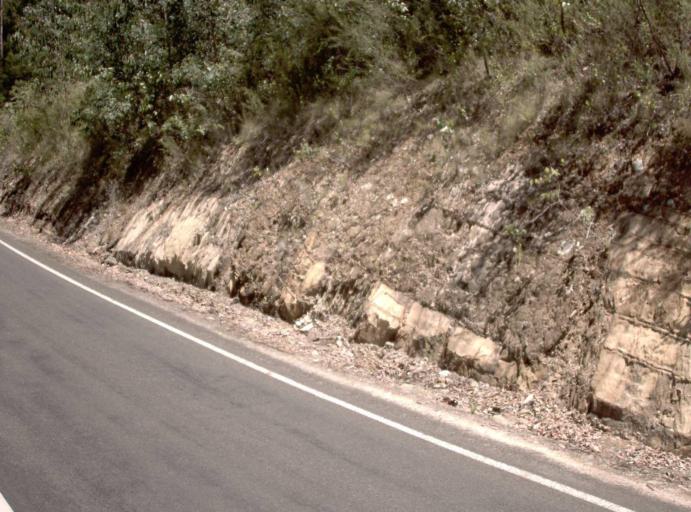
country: AU
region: Victoria
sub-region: East Gippsland
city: Lakes Entrance
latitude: -37.6226
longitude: 147.8826
